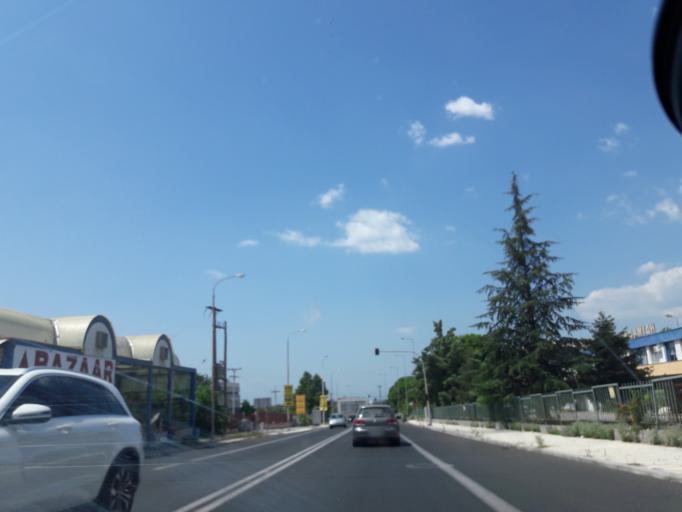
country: GR
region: Central Macedonia
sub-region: Nomos Thessalonikis
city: Thermi
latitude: 40.5409
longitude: 23.0251
